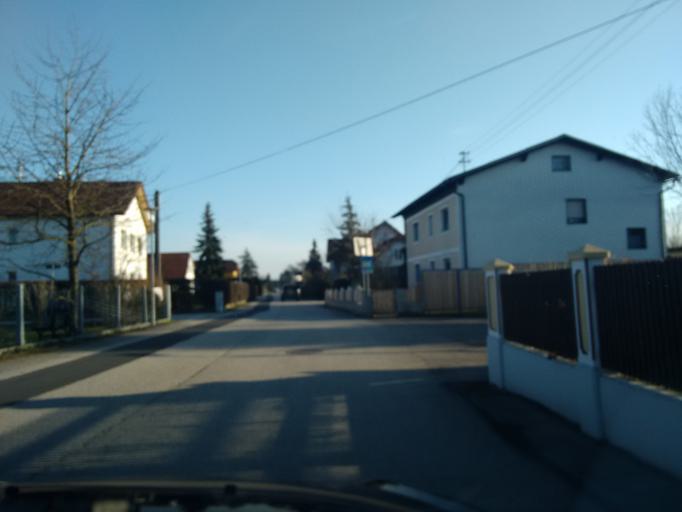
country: AT
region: Upper Austria
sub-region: Wels-Land
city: Marchtrenk
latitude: 48.2028
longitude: 14.1427
